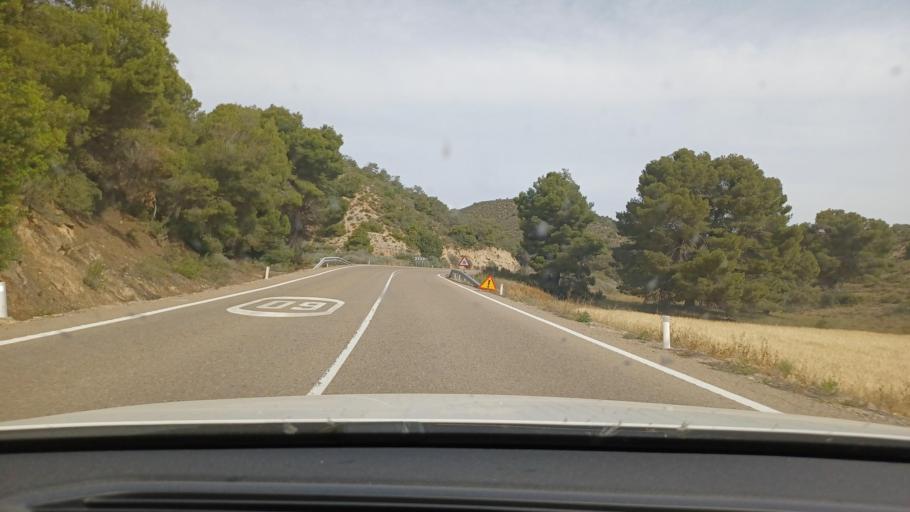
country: ES
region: Aragon
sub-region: Provincia de Zaragoza
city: Chiprana
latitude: 41.3517
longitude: -0.0939
